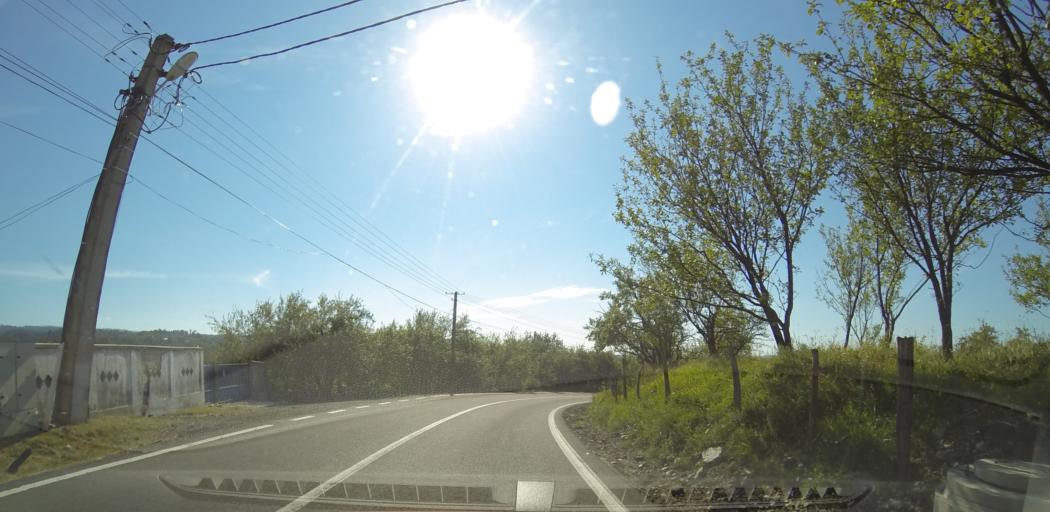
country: RO
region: Gorj
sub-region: Comuna Polovragi
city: Polovragi
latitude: 45.1760
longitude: 23.8591
